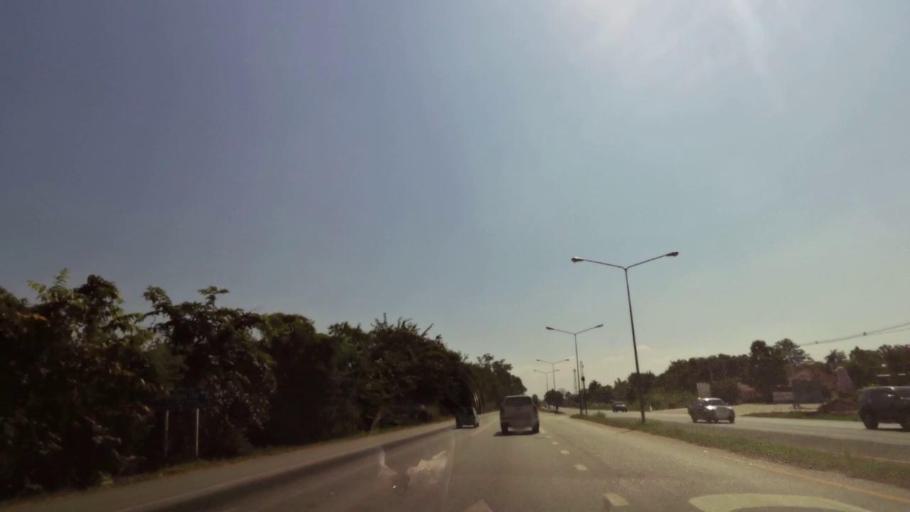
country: TH
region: Nakhon Sawan
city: Kao Liao
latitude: 15.8131
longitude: 100.1201
